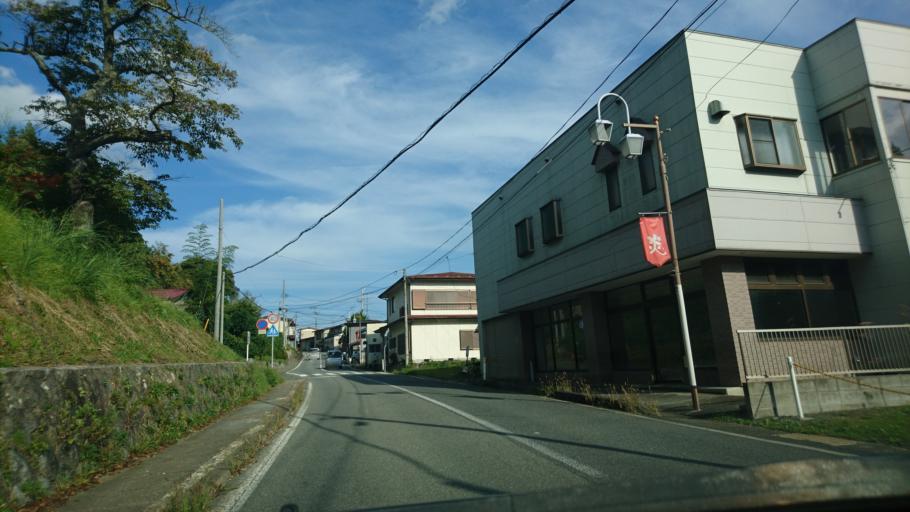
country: JP
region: Iwate
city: Ichinoseki
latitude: 38.8595
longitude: 141.3431
